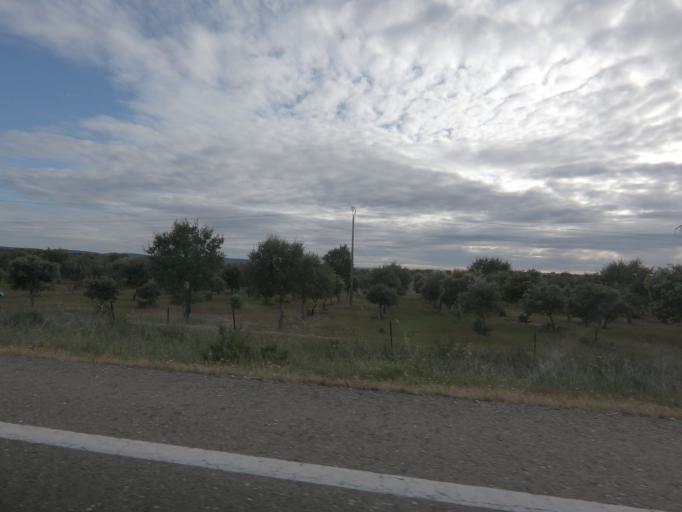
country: ES
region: Extremadura
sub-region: Provincia de Caceres
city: Torrejoncillo
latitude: 39.9278
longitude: -6.5019
